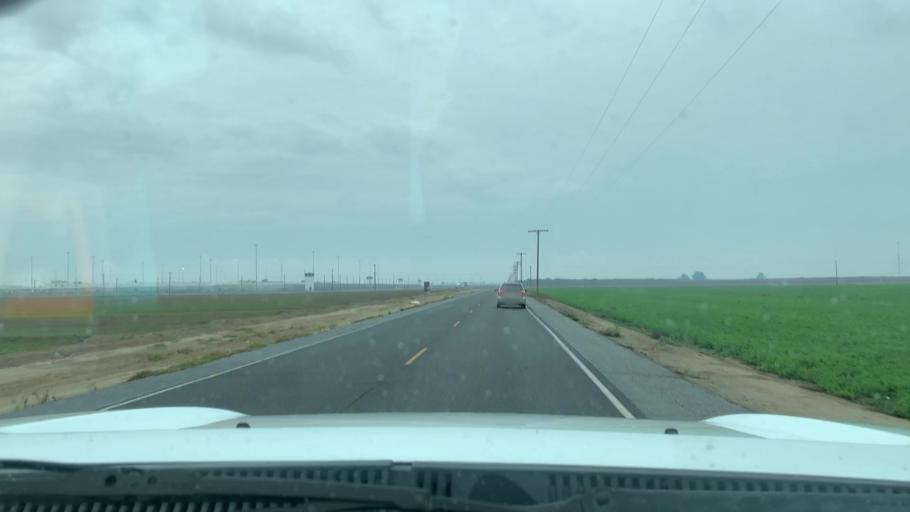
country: US
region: California
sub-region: Kern County
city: Delano
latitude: 35.7612
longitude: -119.3336
